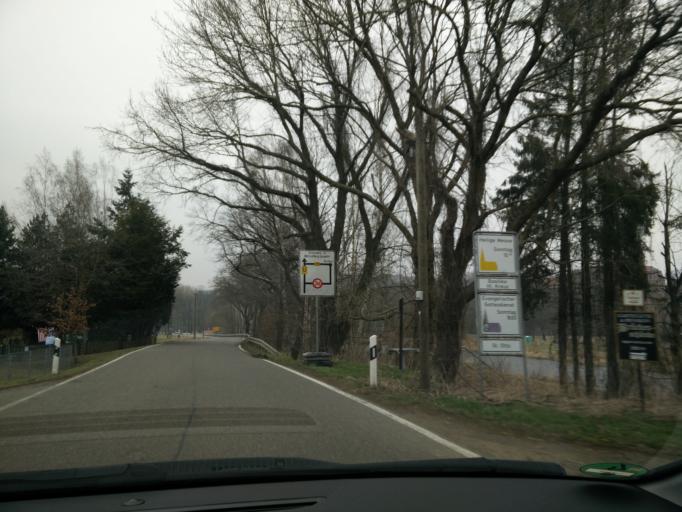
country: DE
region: Saxony
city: Wechselburg
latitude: 51.0009
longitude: 12.7695
